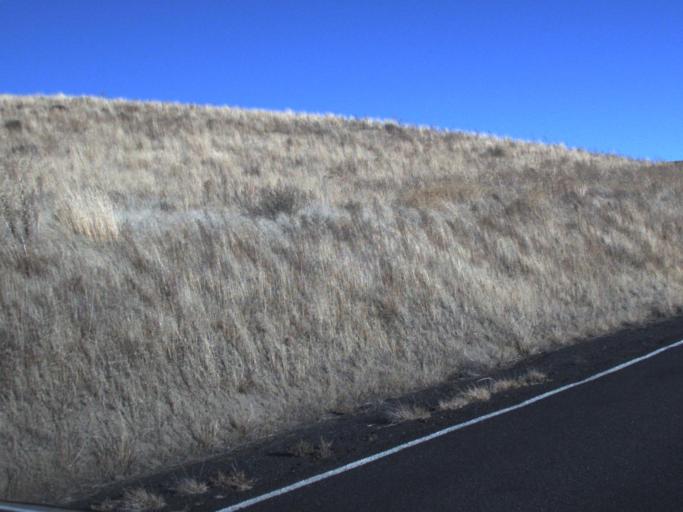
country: US
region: Washington
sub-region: Adams County
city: Ritzville
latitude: 46.6813
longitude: -118.3802
